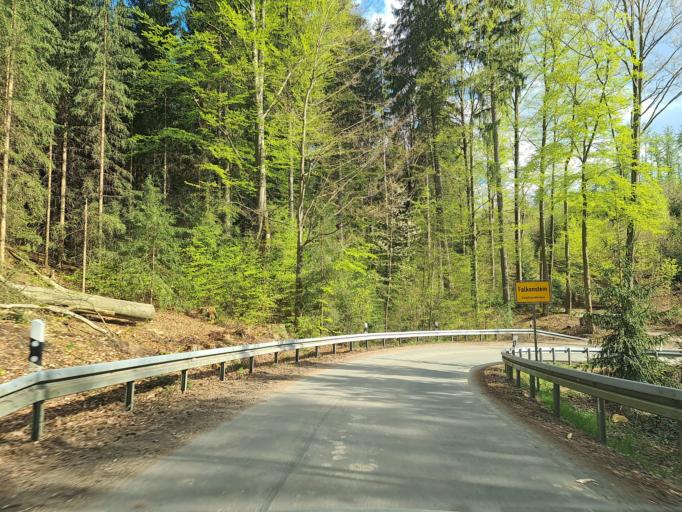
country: DE
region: Saxony
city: Falkenstein
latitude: 50.4682
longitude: 12.3824
